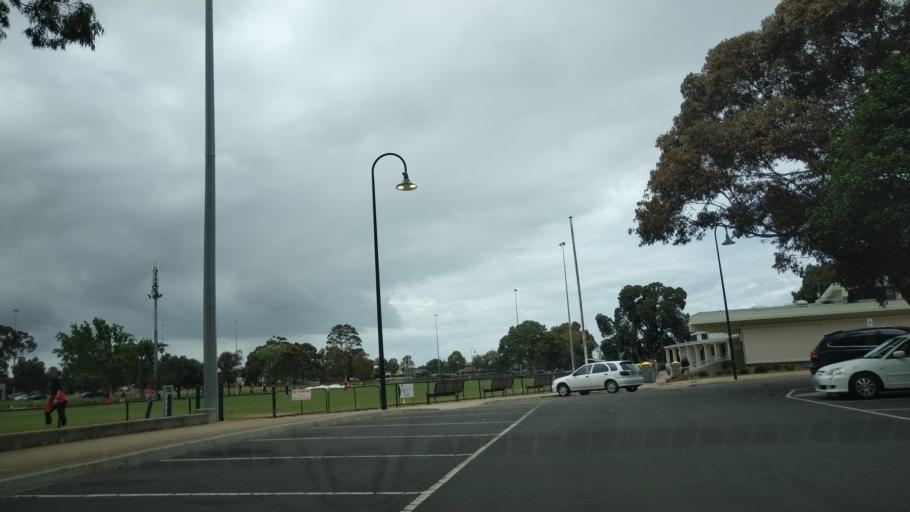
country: AU
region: Victoria
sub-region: Glen Eira
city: Caulfield South
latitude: -37.8929
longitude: 145.0246
